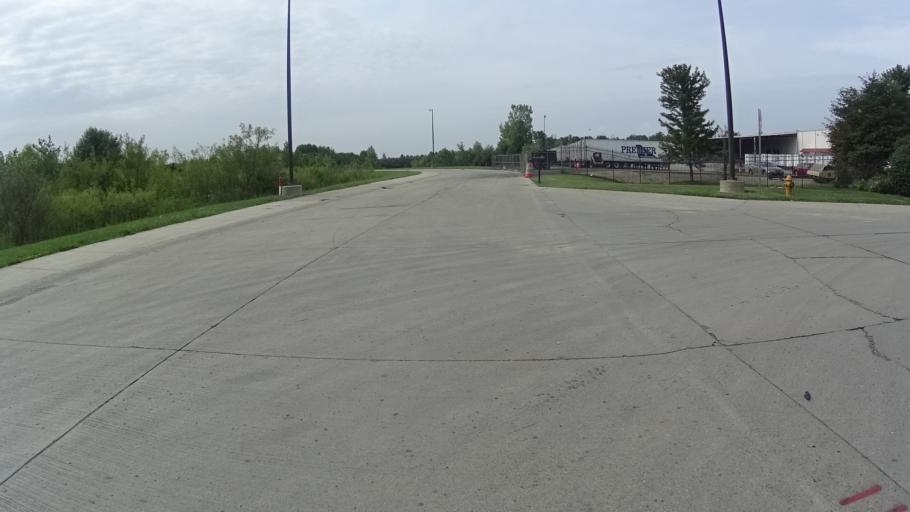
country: US
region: Indiana
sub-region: Madison County
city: Pendleton
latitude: 40.0004
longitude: -85.7710
